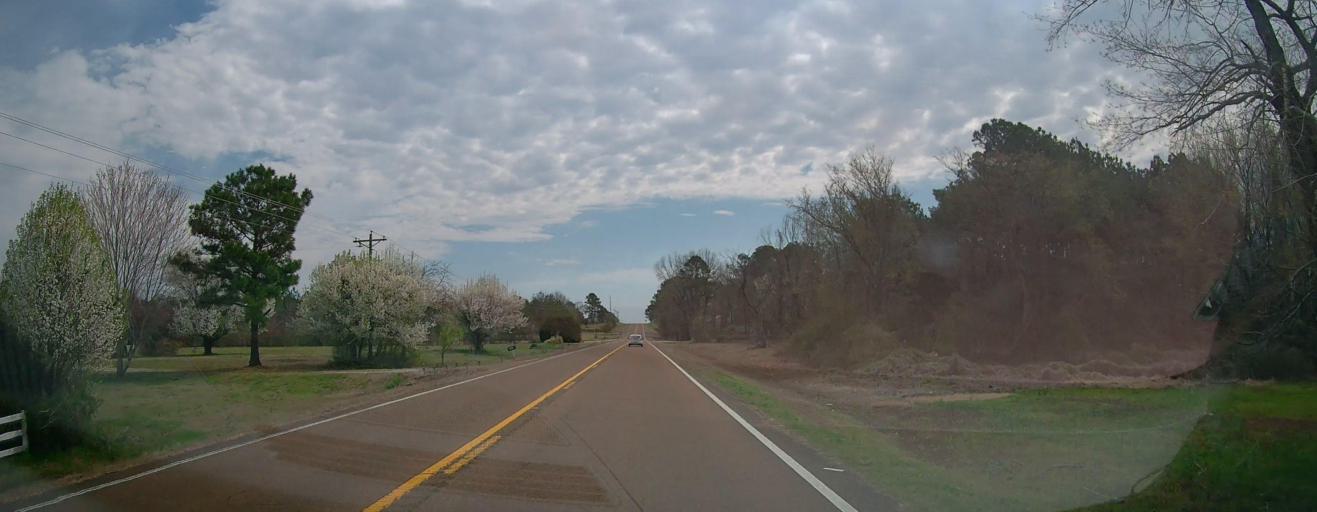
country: US
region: Mississippi
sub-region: Marshall County
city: Holly Springs
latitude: 34.8180
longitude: -89.5350
